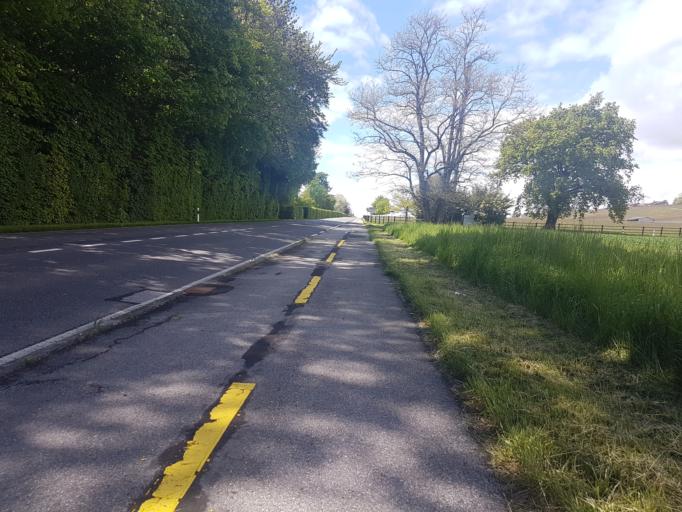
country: CH
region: Vaud
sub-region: Nyon District
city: Rolle
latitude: 46.4419
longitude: 6.3164
